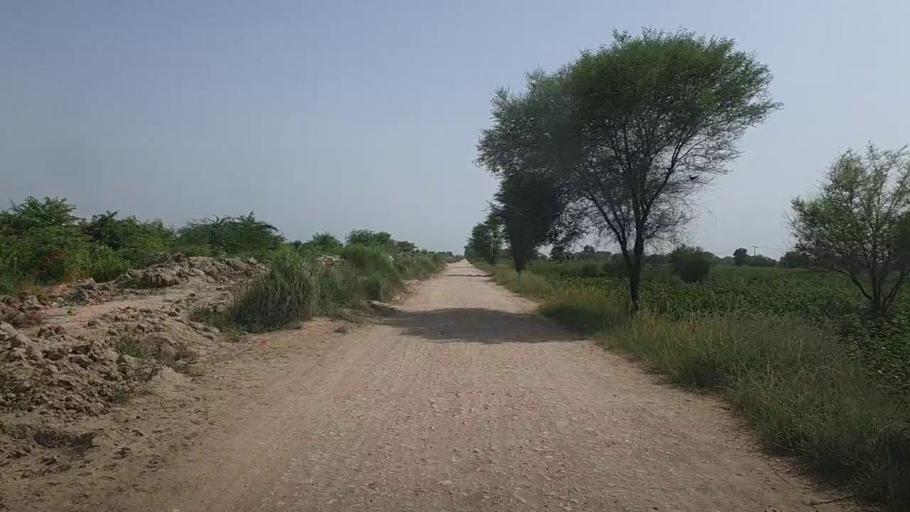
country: PK
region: Sindh
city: Pad Idan
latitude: 26.7923
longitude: 68.3282
